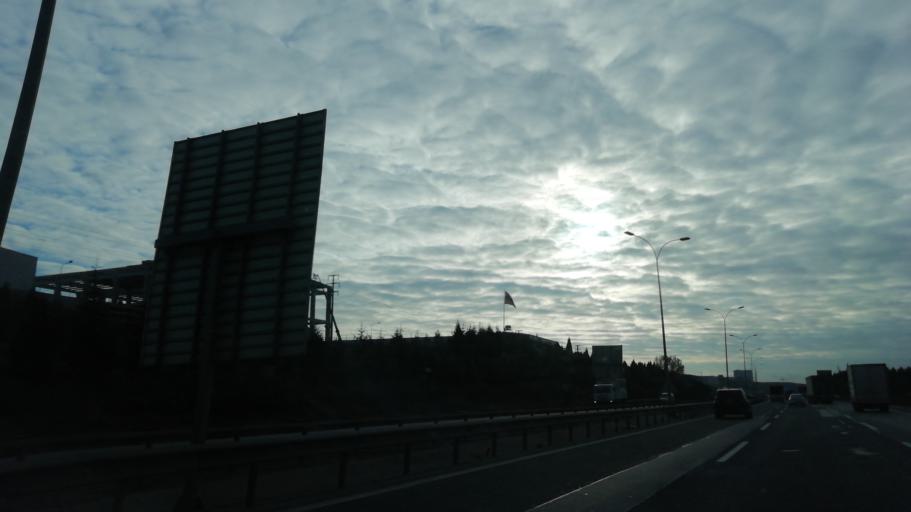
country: TR
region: Kocaeli
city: Balcik
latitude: 40.8634
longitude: 29.4008
